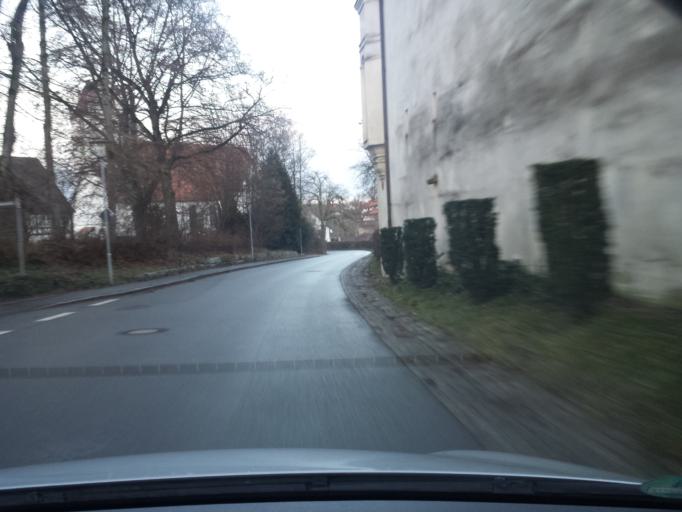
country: DE
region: Baden-Wuerttemberg
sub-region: Tuebingen Region
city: Mittelbiberach
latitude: 48.0863
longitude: 9.7492
